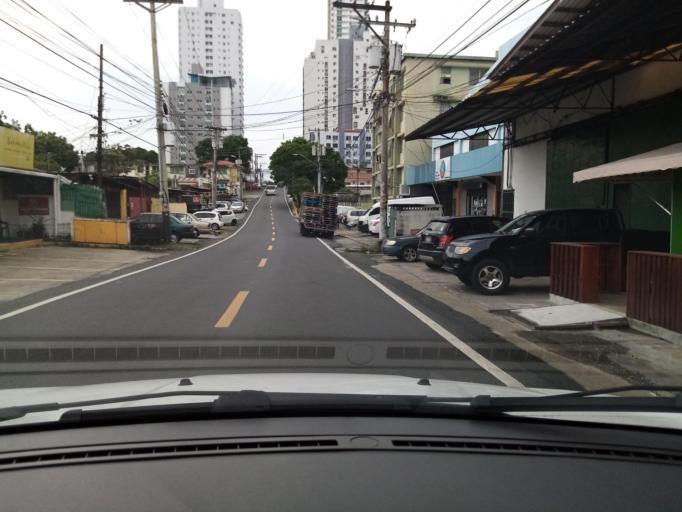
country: PA
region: Panama
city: Panama
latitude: 9.0078
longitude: -79.5070
